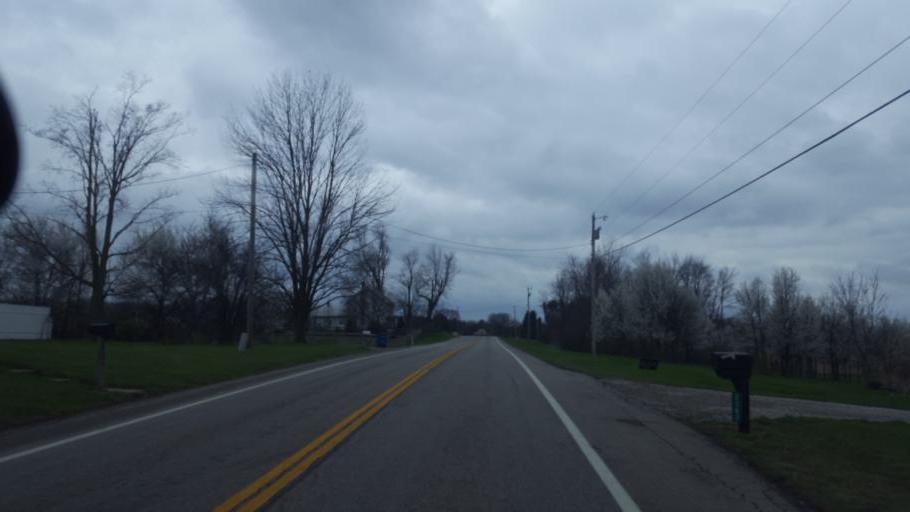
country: US
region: Ohio
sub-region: Delaware County
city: Sunbury
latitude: 40.2714
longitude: -82.8522
